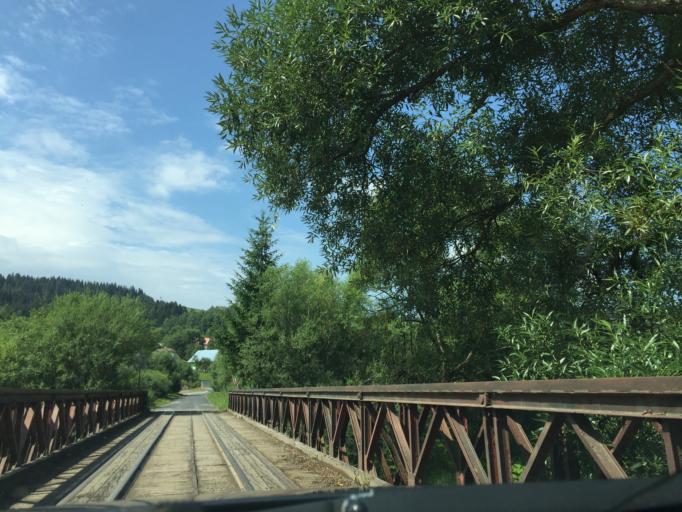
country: PL
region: Silesian Voivodeship
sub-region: Powiat zywiecki
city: Korbielow
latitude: 49.4342
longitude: 19.3159
